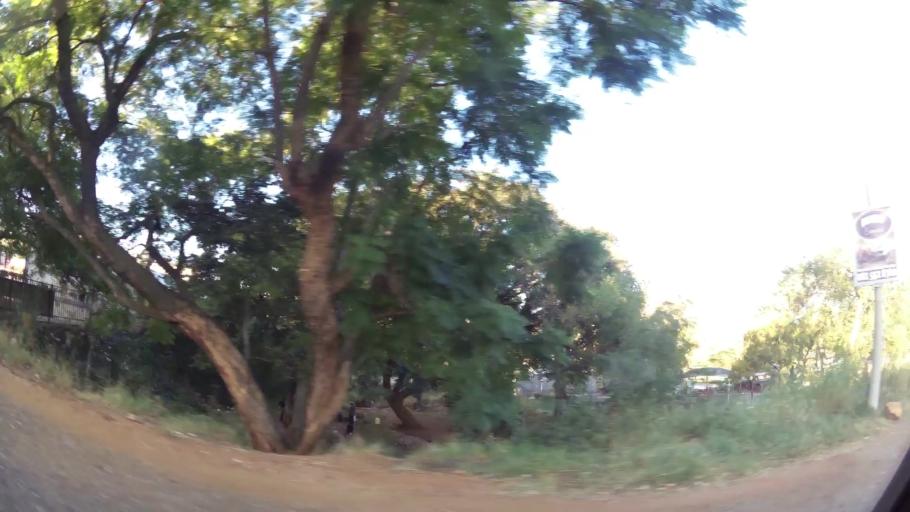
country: ZA
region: North-West
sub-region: Bojanala Platinum District Municipality
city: Rustenburg
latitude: -25.7094
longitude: 27.2400
